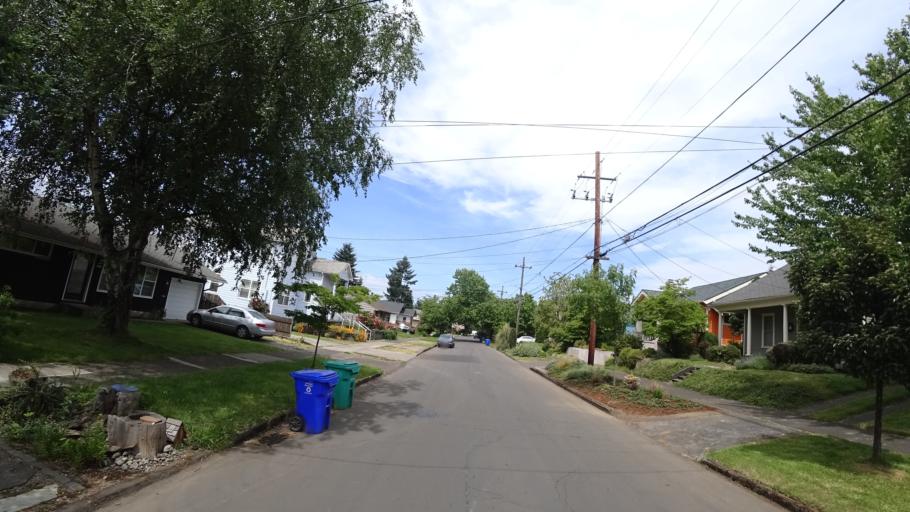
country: US
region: Oregon
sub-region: Washington County
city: West Haven
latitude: 45.5946
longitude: -122.7628
